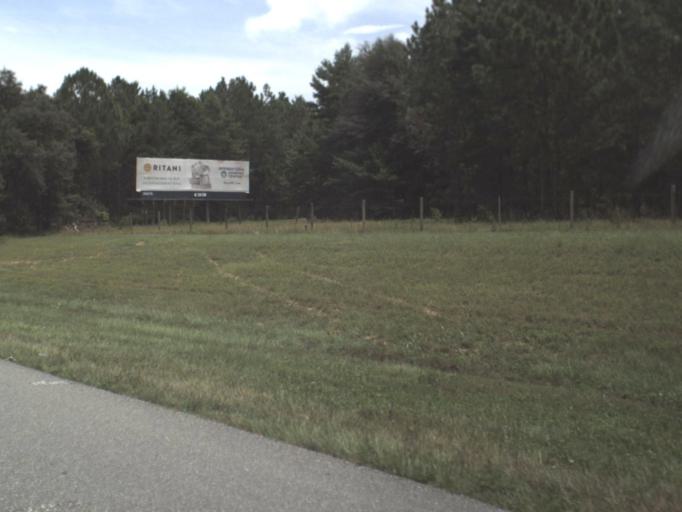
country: US
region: Florida
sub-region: Hernando County
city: Hill 'n Dale
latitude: 28.5037
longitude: -82.2456
